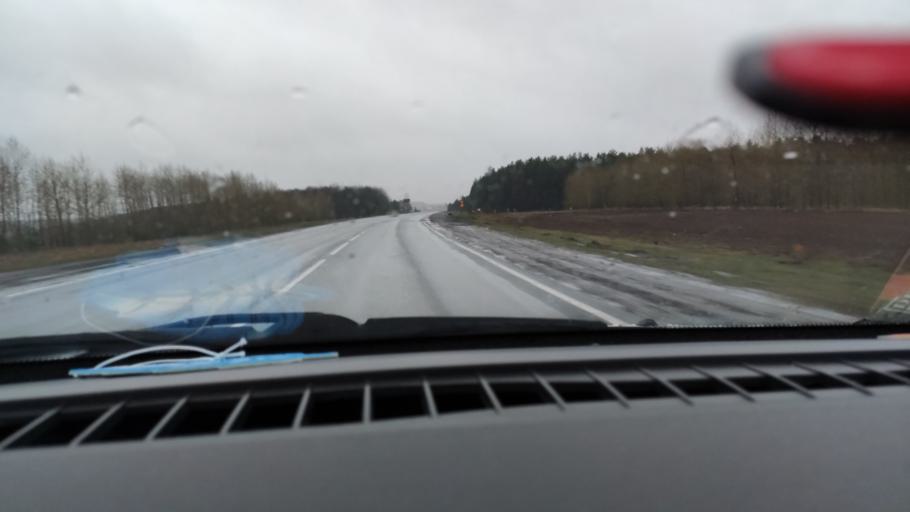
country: RU
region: Tatarstan
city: Mendeleyevsk
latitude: 55.9475
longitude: 52.2990
